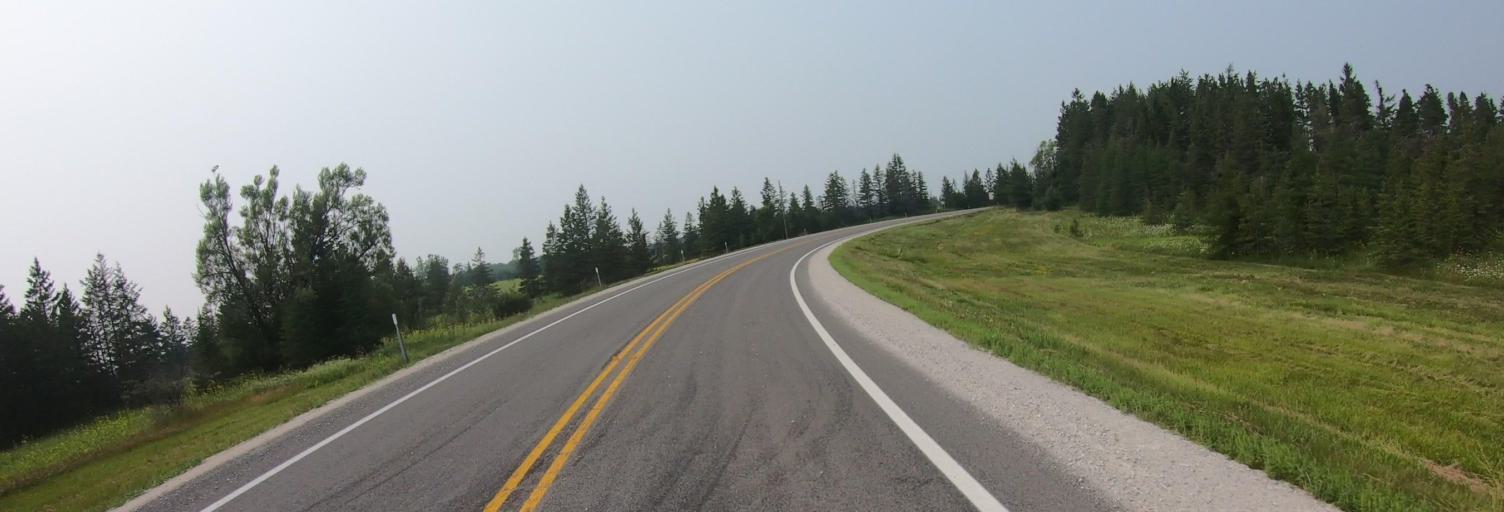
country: US
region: Michigan
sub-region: Chippewa County
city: Sault Ste. Marie
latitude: 46.0721
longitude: -84.2380
